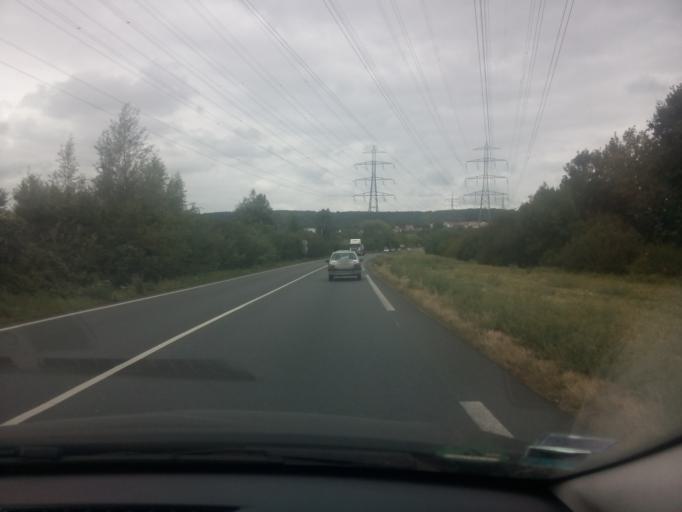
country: FR
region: Ile-de-France
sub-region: Departement de l'Essonne
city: Igny
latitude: 48.7327
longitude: 2.2348
